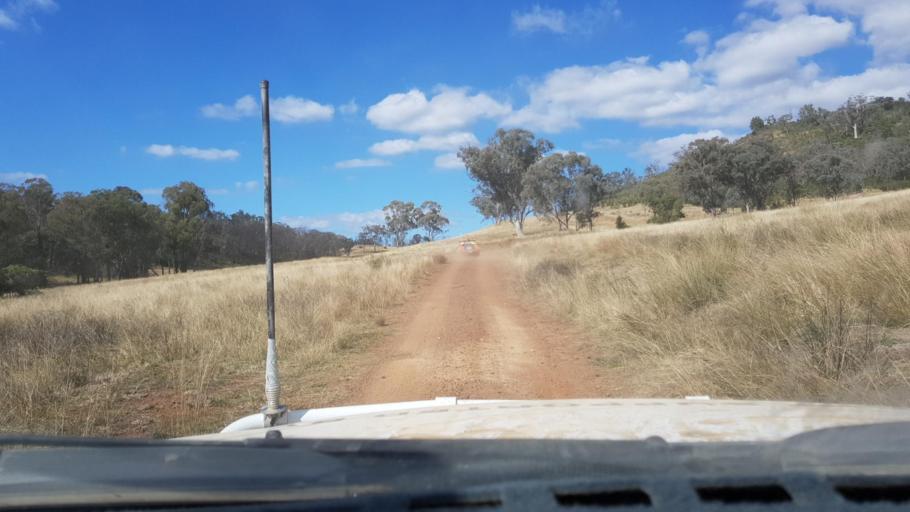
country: AU
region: New South Wales
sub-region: Tamworth Municipality
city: Manilla
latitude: -30.4324
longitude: 150.8234
